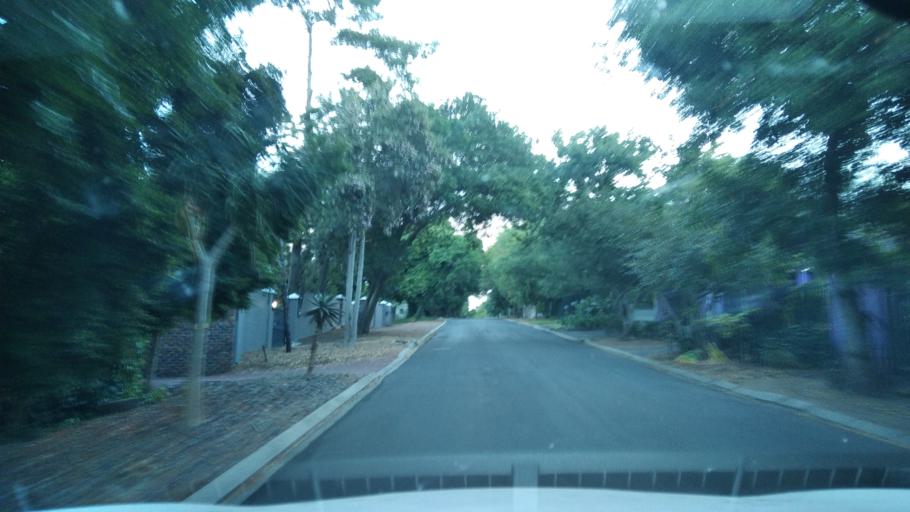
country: ZA
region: Western Cape
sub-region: City of Cape Town
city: Kraaifontein
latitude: -33.8203
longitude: 18.6606
